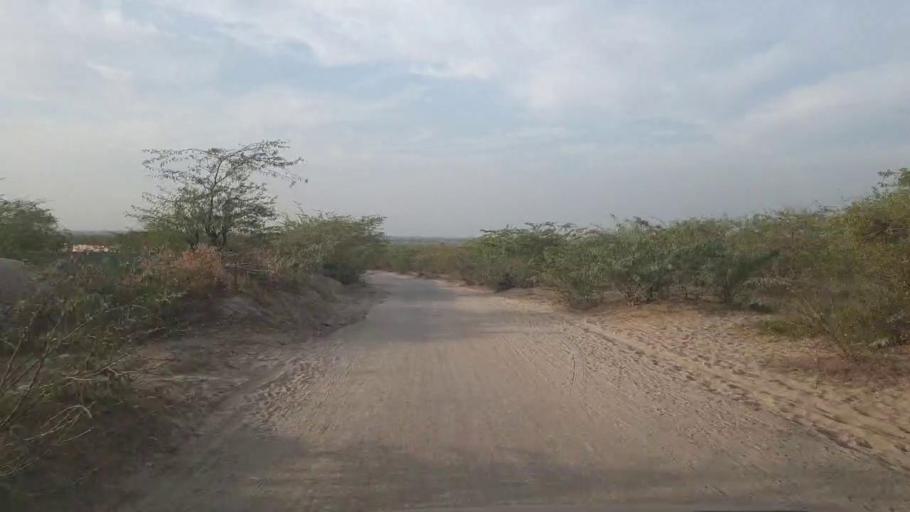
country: PK
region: Sindh
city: Nabisar
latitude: 25.1458
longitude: 69.6722
